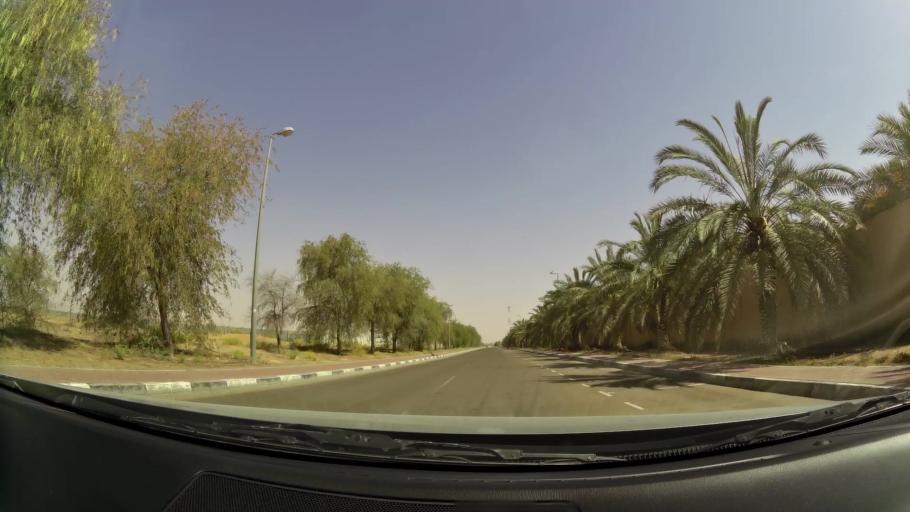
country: OM
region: Al Buraimi
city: Al Buraymi
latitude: 24.2952
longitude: 55.7526
